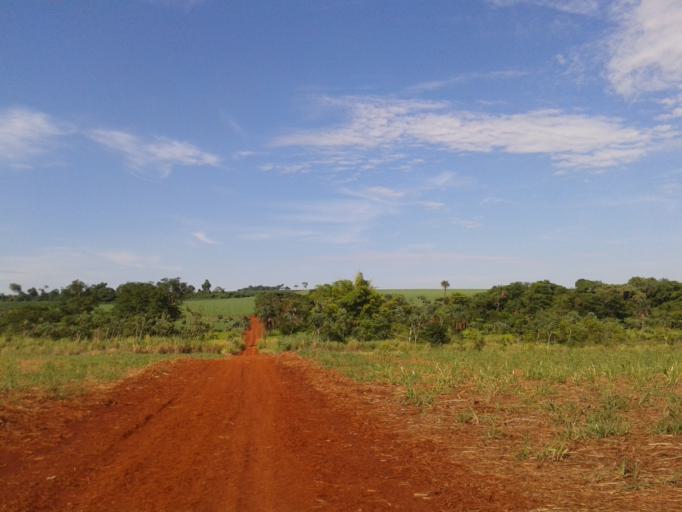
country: BR
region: Minas Gerais
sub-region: Centralina
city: Centralina
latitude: -18.6363
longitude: -49.2551
